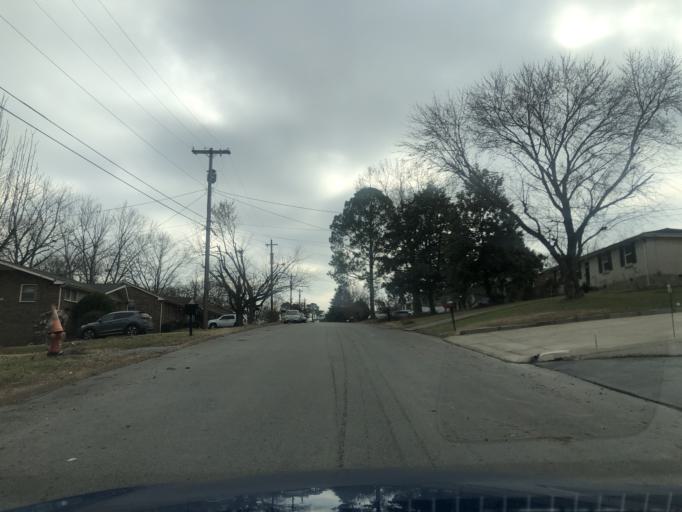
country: US
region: Tennessee
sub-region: Davidson County
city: Oak Hill
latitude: 36.0915
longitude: -86.7162
